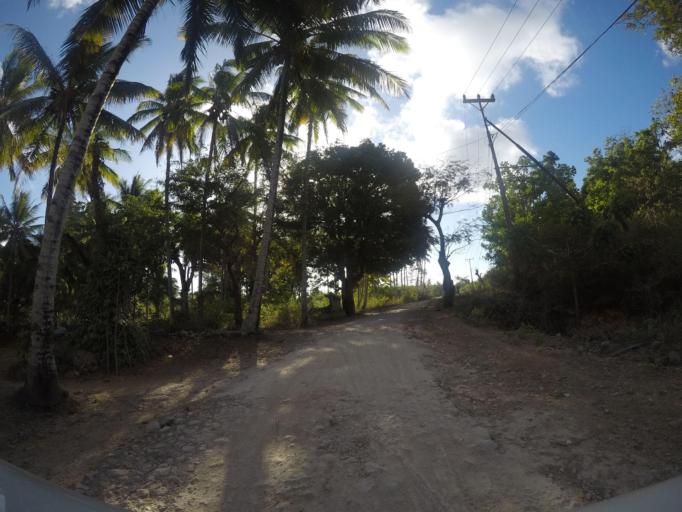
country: TL
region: Lautem
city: Lospalos
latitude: -8.4526
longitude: 126.8835
